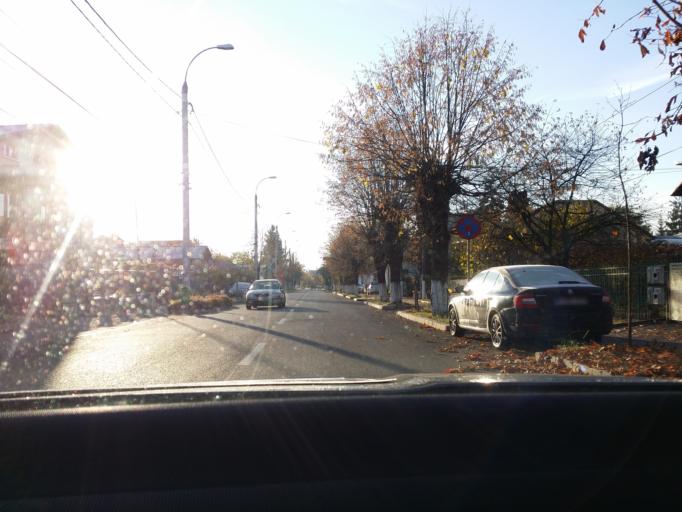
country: RO
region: Prahova
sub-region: Municipiul Campina
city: Campina
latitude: 45.1370
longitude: 25.7264
